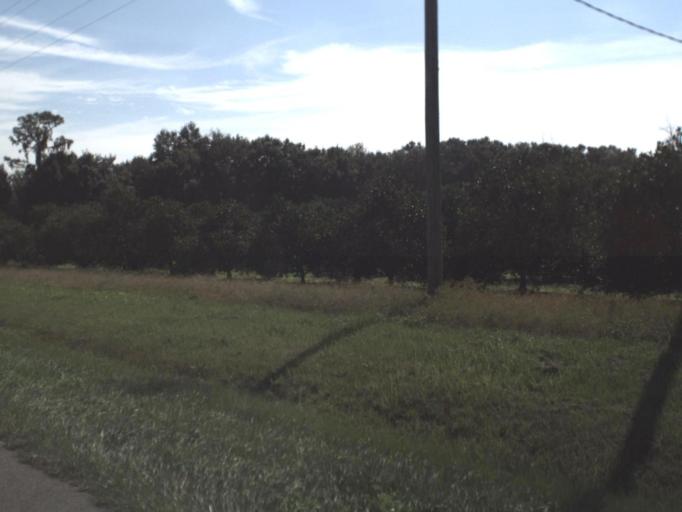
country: US
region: Florida
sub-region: Hardee County
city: Wauchula
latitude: 27.5514
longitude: -81.7330
